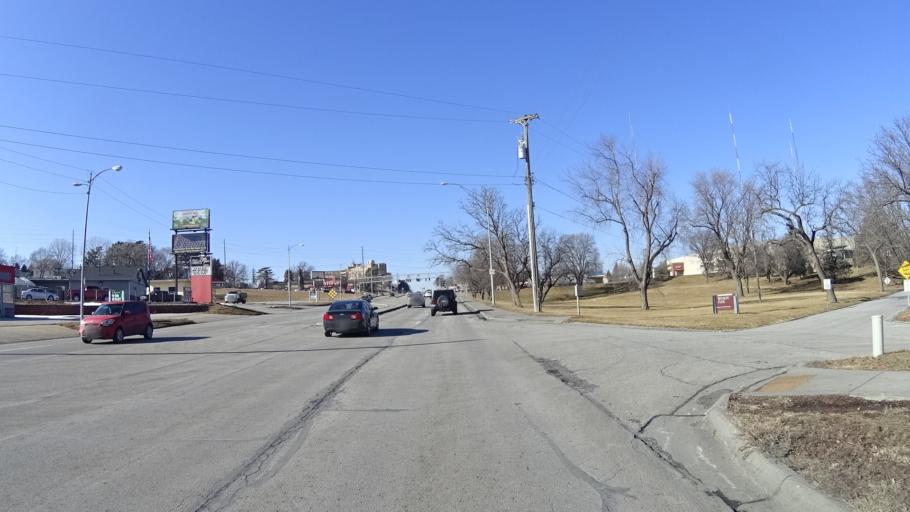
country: US
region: Nebraska
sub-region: Douglas County
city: Omaha
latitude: 41.2963
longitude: -96.0212
